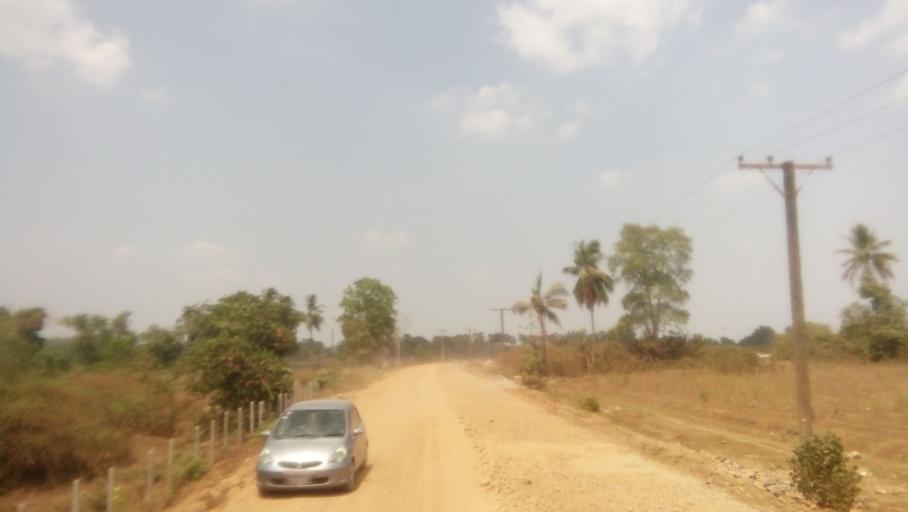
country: MM
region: Kayin
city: Hpa-an
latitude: 17.1359
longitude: 97.8143
